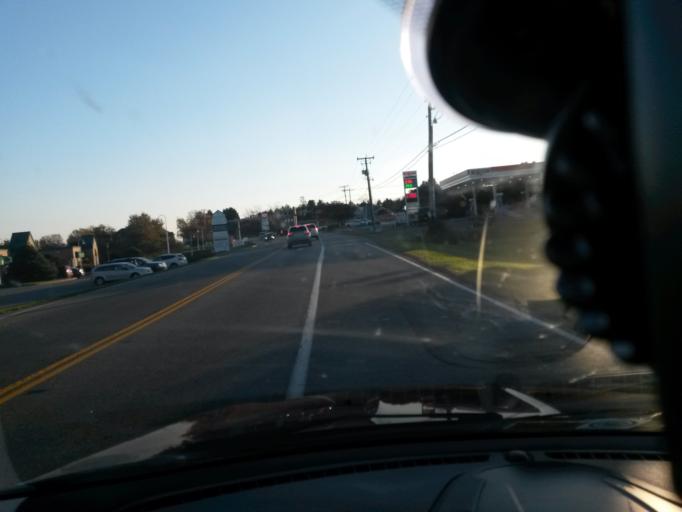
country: US
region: Virginia
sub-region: Franklin County
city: North Shore
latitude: 37.1197
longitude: -79.7147
